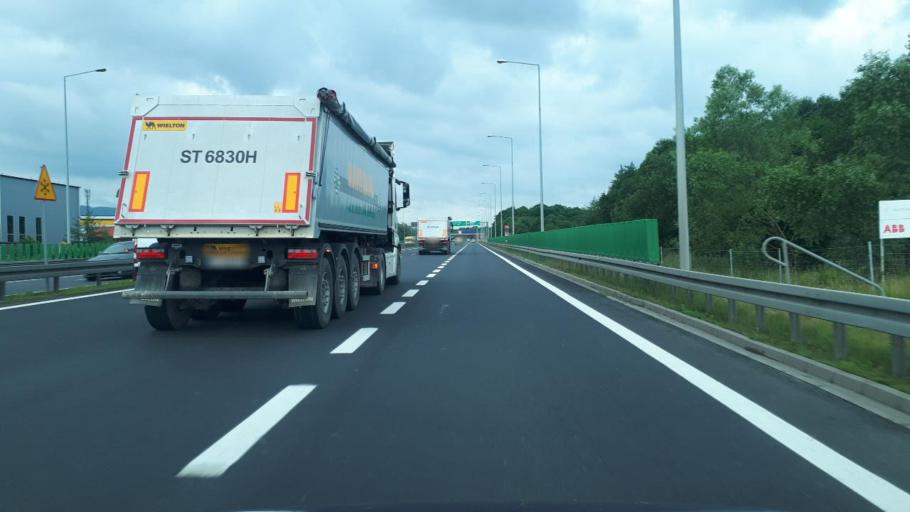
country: PL
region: Silesian Voivodeship
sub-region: Powiat bielski
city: Mazancowice
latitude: 49.8336
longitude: 18.9725
